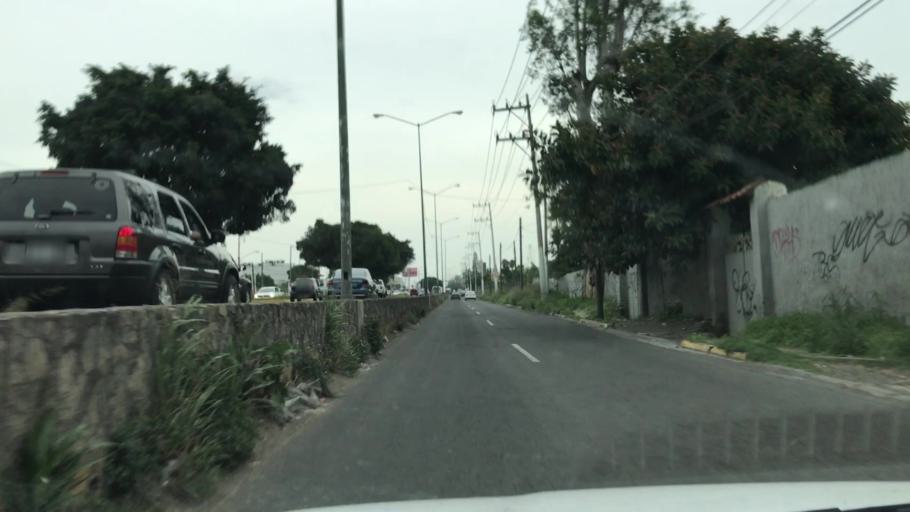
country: MX
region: Jalisco
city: Nuevo Mexico
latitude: 20.7526
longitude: -103.4233
